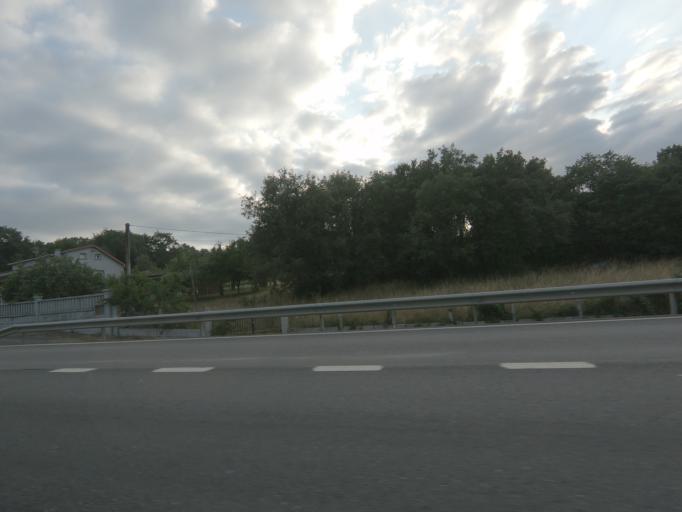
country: ES
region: Galicia
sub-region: Provincia de Ourense
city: Taboadela
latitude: 42.2442
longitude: -7.8427
